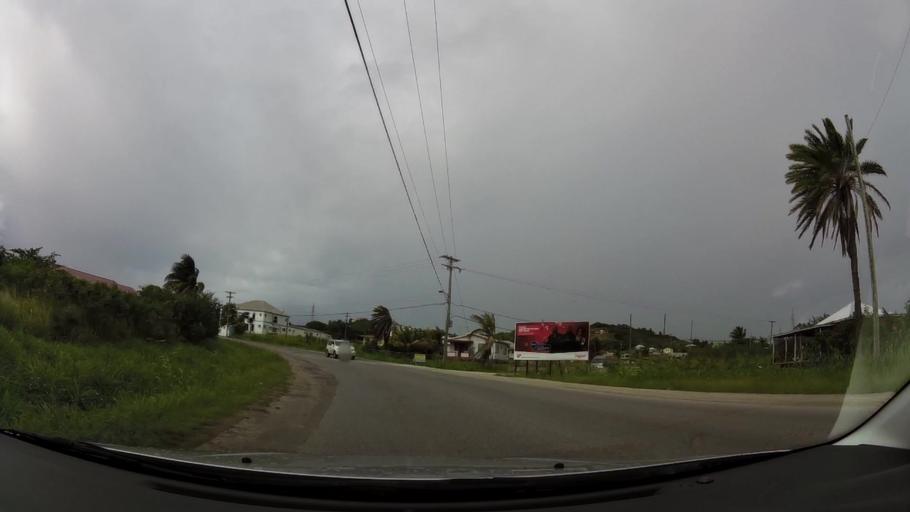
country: AG
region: Saint John
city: Potters Village
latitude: 17.0939
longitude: -61.8175
